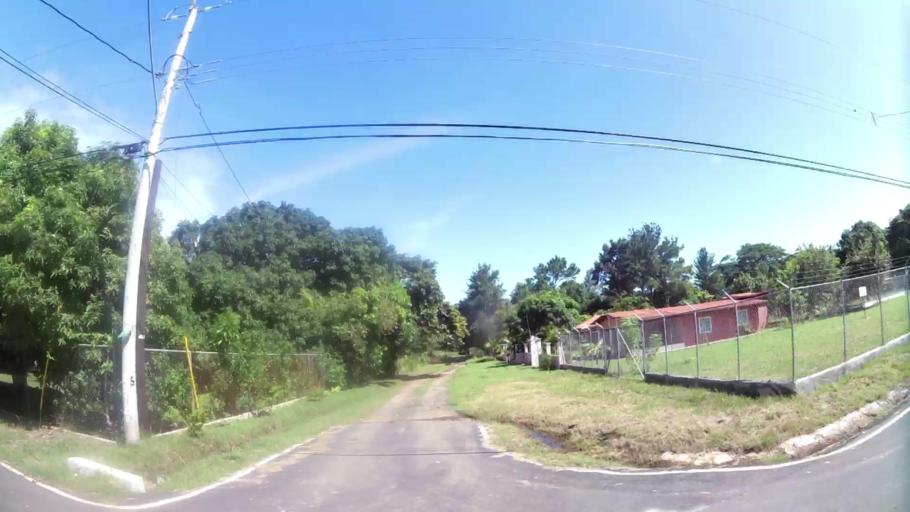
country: PA
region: Panama
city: Nueva Gorgona
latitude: 8.5596
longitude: -79.8752
